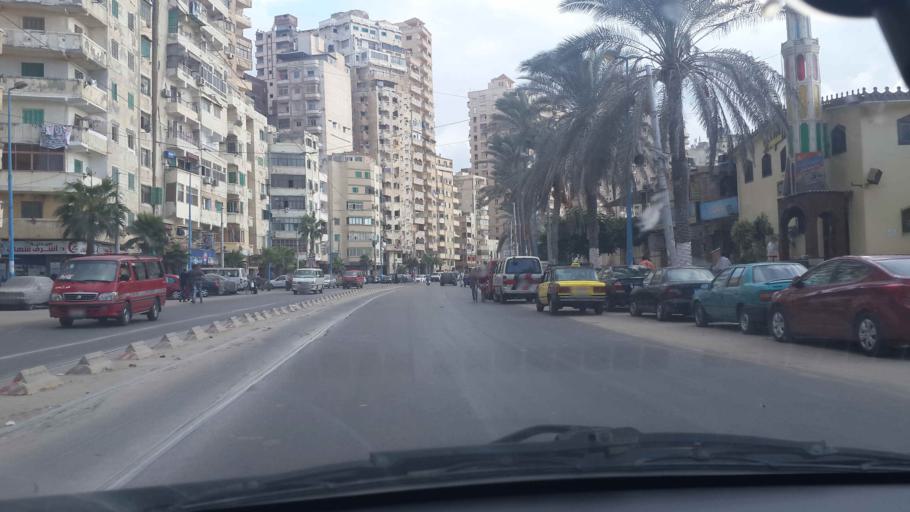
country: EG
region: Alexandria
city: Alexandria
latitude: 31.2072
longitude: 29.8790
